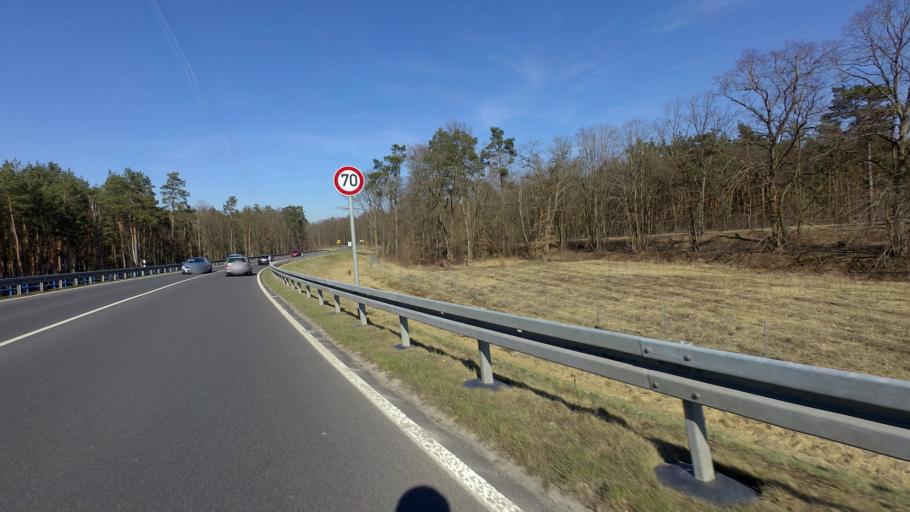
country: DE
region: Brandenburg
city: Eberswalde
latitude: 52.8581
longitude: 13.8297
